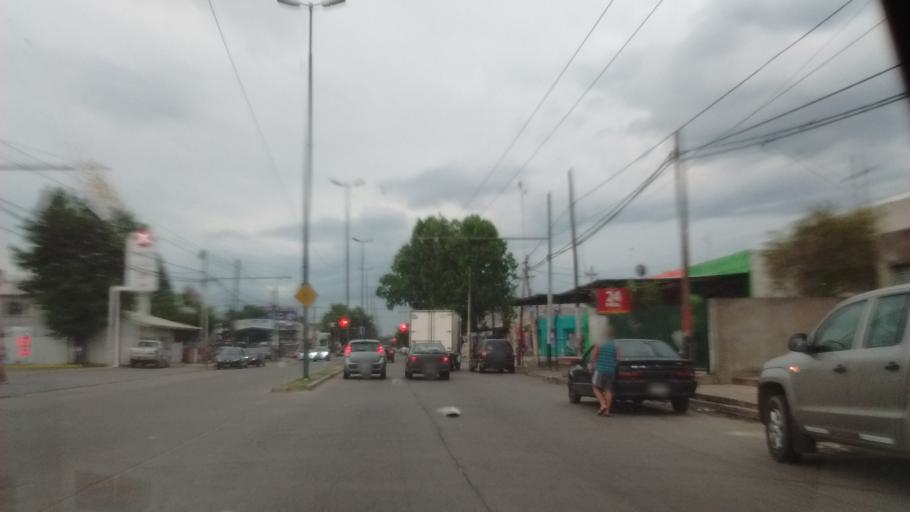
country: AR
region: Santa Fe
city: Perez
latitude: -32.9406
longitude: -60.7253
